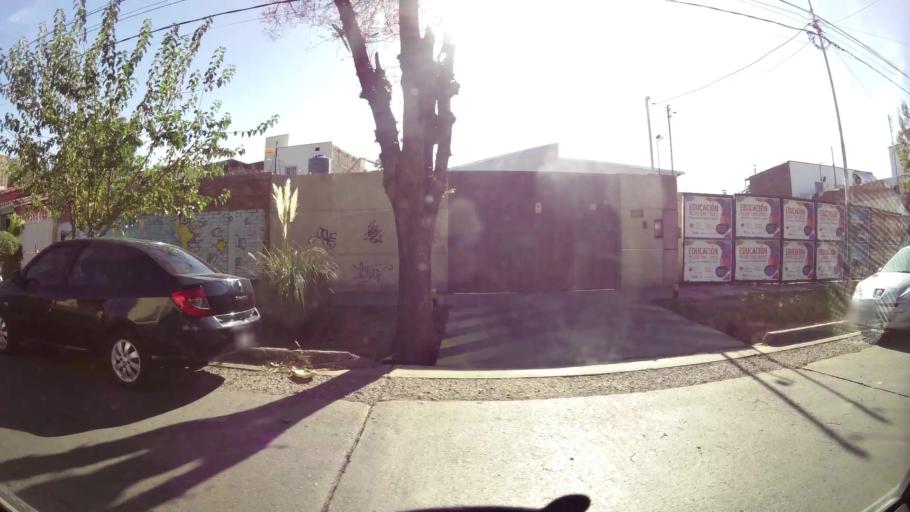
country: AR
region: Mendoza
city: Mendoza
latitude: -32.9061
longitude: -68.8251
